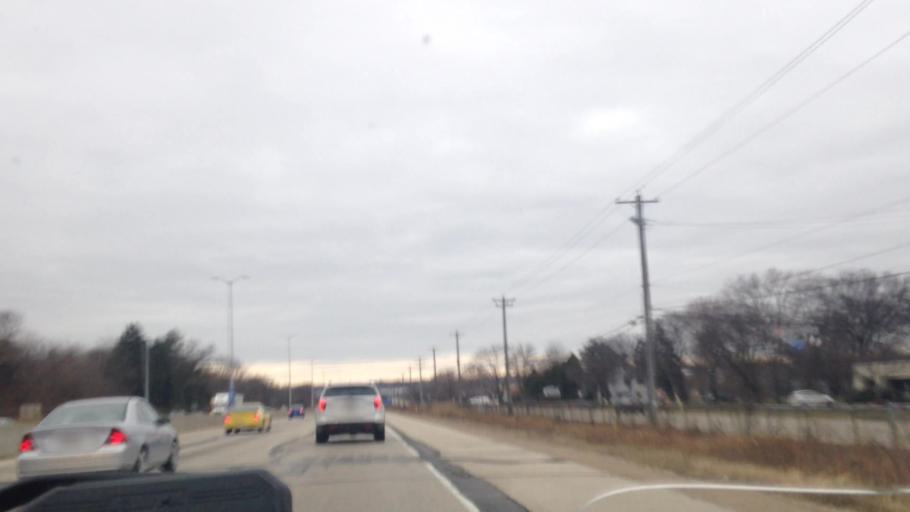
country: US
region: Wisconsin
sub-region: Waukesha County
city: Menomonee Falls
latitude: 43.1685
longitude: -88.0756
